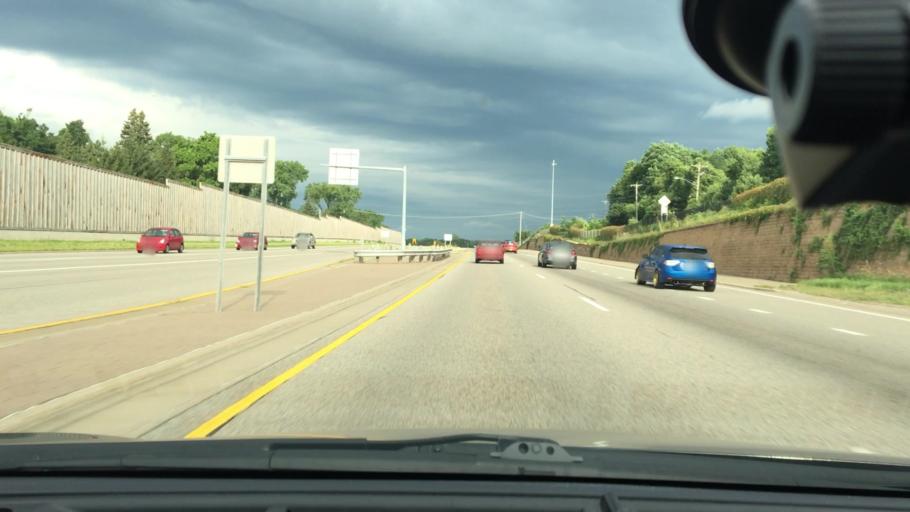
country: US
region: Minnesota
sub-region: Hennepin County
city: Golden Valley
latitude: 44.9847
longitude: -93.3517
